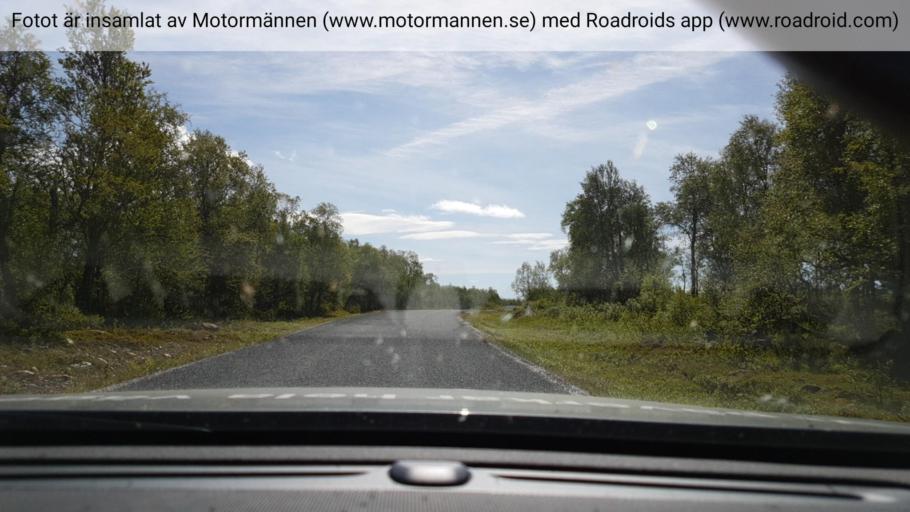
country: NO
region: Nordland
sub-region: Hattfjelldal
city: Hattfjelldal
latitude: 65.3902
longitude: 15.0136
